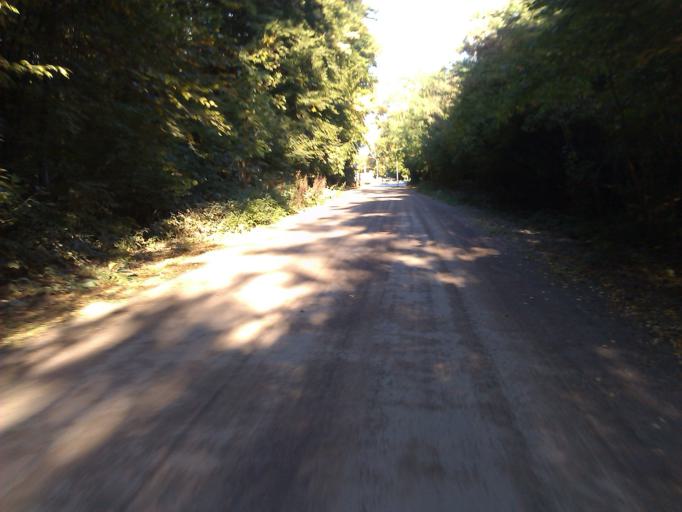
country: DE
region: Hesse
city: Morfelden-Walldorf
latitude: 50.0106
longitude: 8.6007
